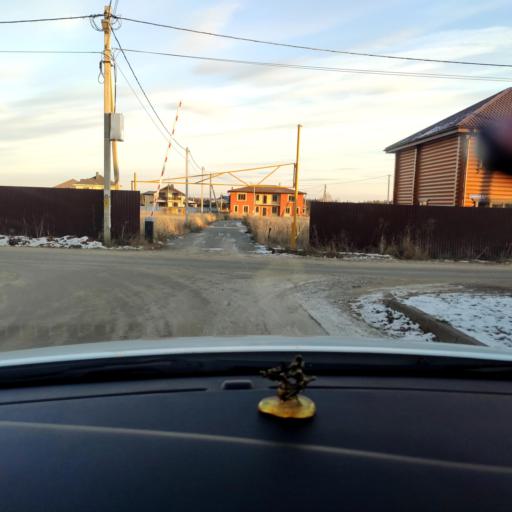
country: RU
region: Tatarstan
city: Stolbishchi
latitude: 55.6057
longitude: 49.1470
